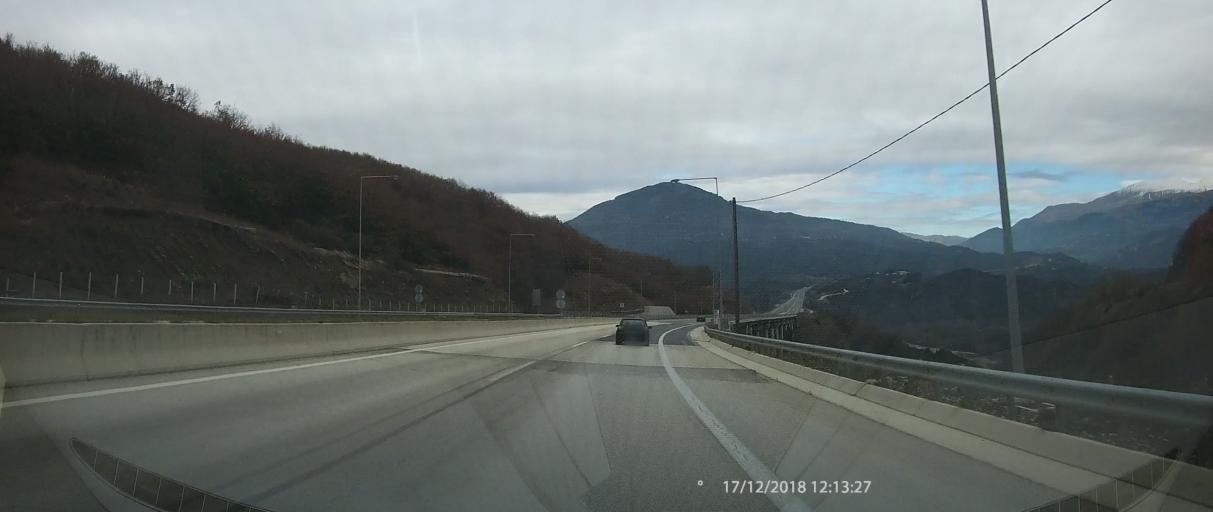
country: GR
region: Epirus
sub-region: Nomos Ioanninon
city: Katsikas
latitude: 39.7063
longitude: 20.9718
